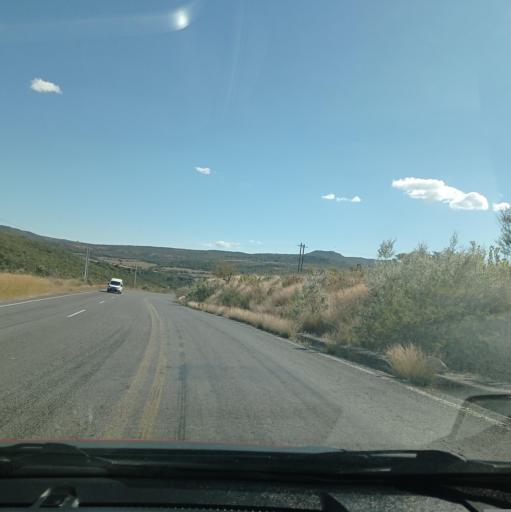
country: MX
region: Jalisco
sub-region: San Julian
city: Colonia Veintitres de Mayo
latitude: 21.0071
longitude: -102.2729
